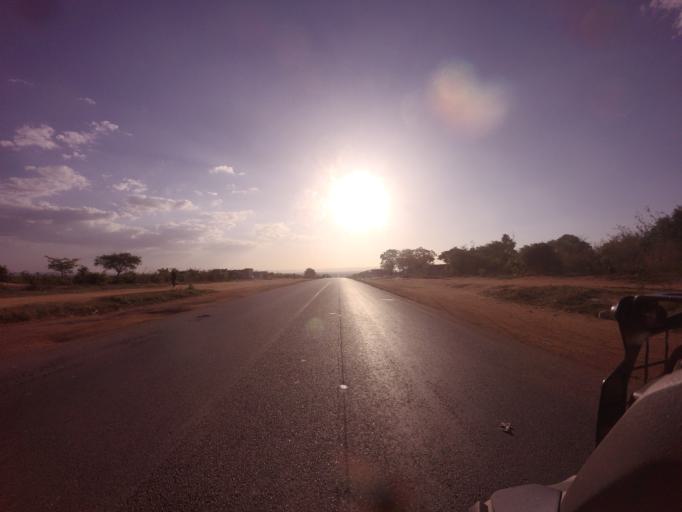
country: AO
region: Huila
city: Lubango
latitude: -14.7888
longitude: 13.7089
